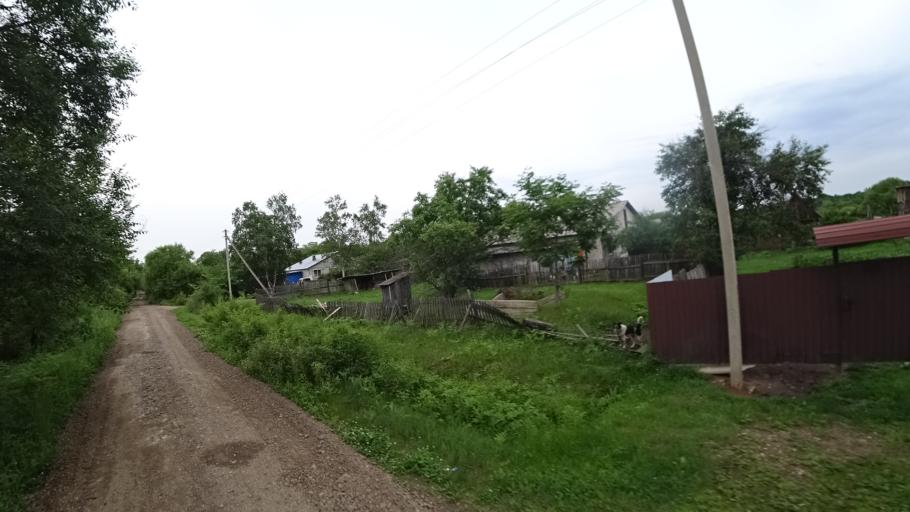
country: RU
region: Primorskiy
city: Novosysoyevka
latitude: 44.2440
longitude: 133.3747
